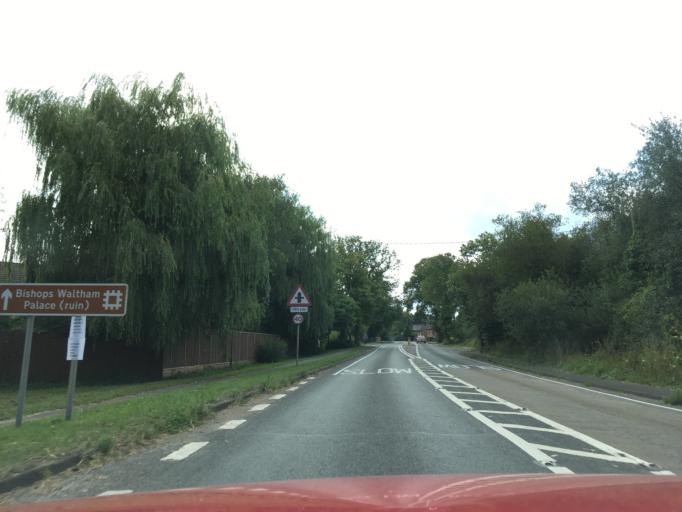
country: GB
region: England
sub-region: Hampshire
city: Bishops Waltham
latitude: 50.9729
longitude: -1.2562
